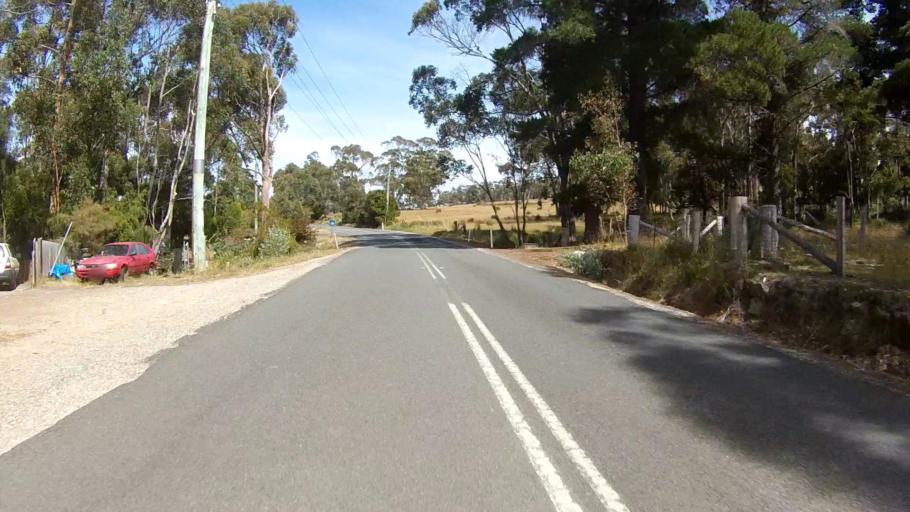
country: AU
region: Tasmania
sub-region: Huon Valley
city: Cygnet
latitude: -43.2738
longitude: 147.1557
